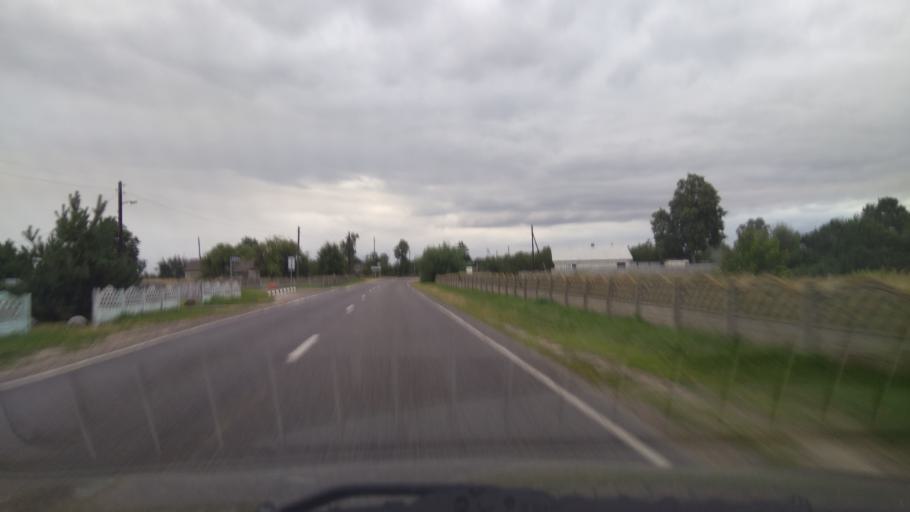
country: BY
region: Brest
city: Byaroza
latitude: 52.4207
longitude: 24.9808
